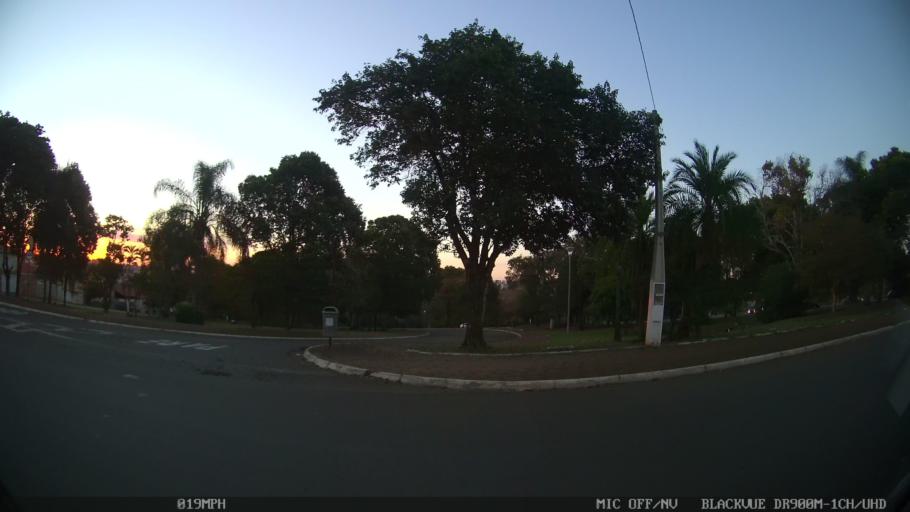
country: BR
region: Sao Paulo
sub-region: Santa Barbara D'Oeste
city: Santa Barbara d'Oeste
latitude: -22.7589
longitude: -47.3995
